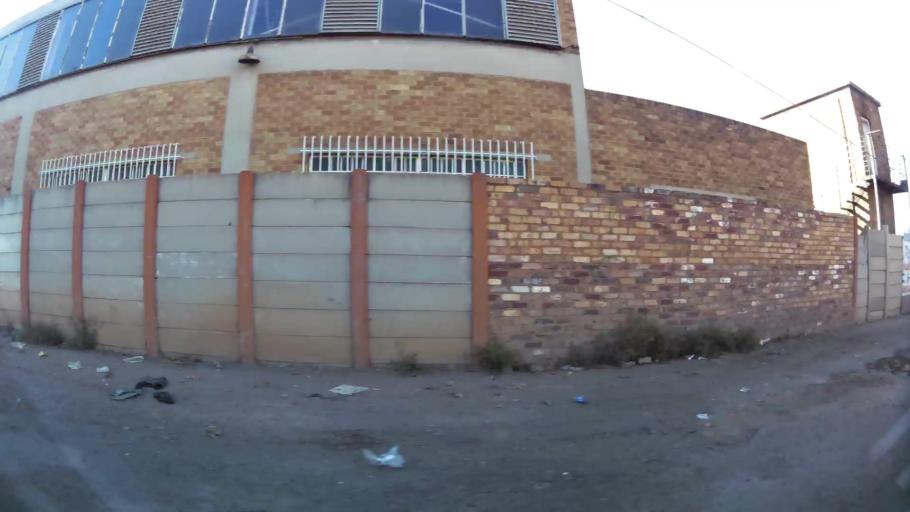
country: ZA
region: Gauteng
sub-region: City of Johannesburg Metropolitan Municipality
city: Johannesburg
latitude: -26.2093
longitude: 27.9917
